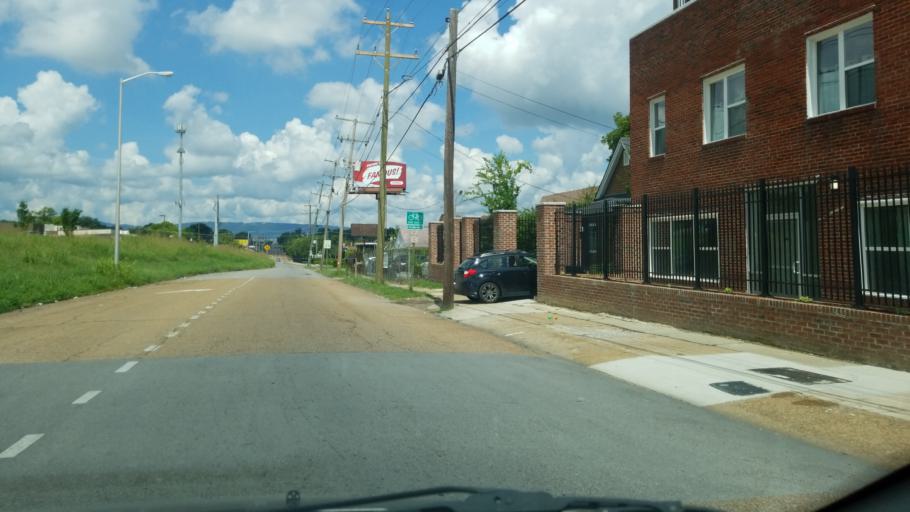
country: US
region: Tennessee
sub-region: Hamilton County
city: East Ridge
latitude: 35.0321
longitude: -85.2642
